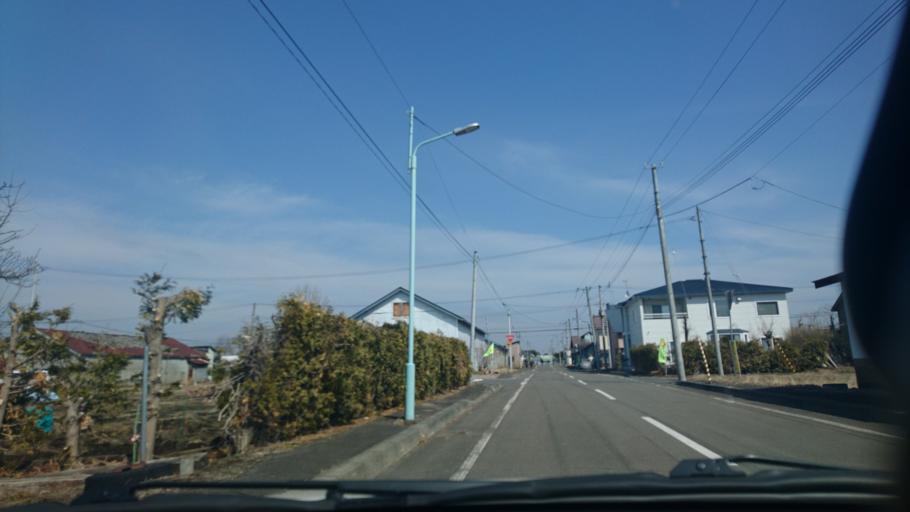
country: JP
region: Hokkaido
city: Otofuke
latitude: 43.0954
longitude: 143.2282
